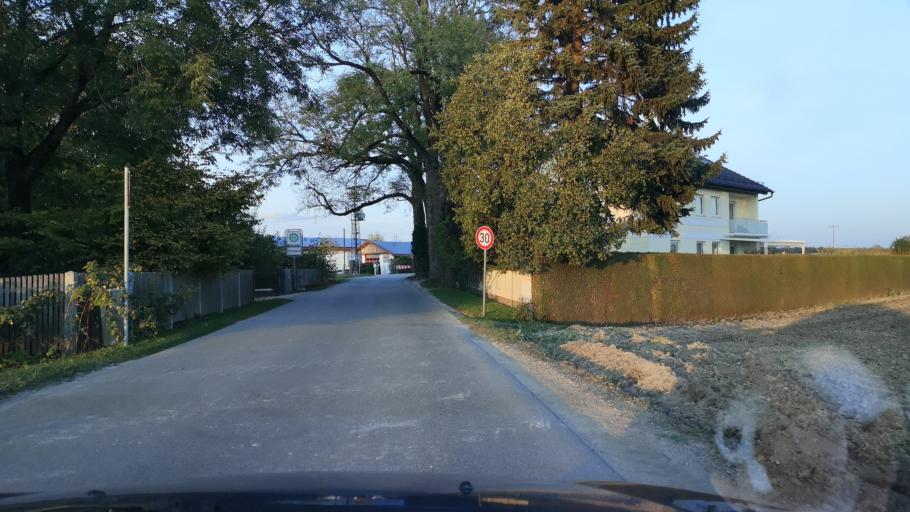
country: DE
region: Bavaria
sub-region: Upper Bavaria
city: Ismaning
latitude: 48.2351
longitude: 11.7160
